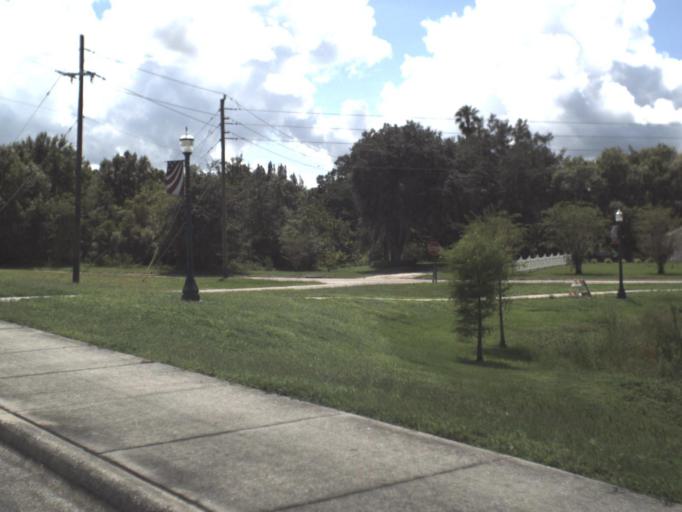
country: US
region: Florida
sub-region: DeSoto County
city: Arcadia
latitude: 27.2187
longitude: -81.8712
